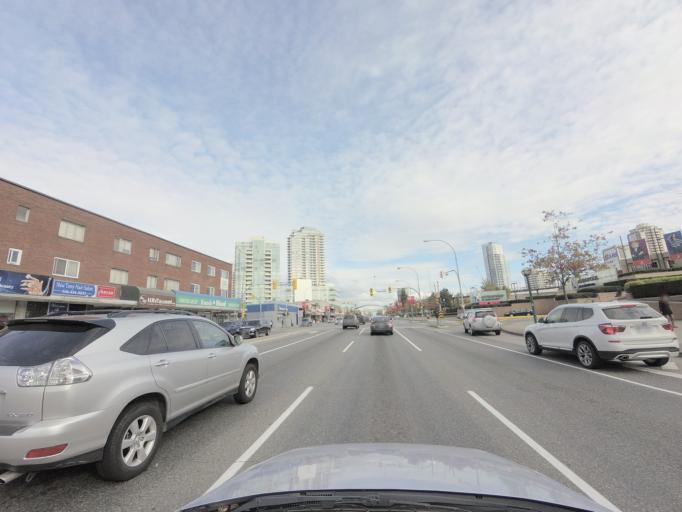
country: CA
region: British Columbia
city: Burnaby
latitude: 49.2285
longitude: -122.9999
